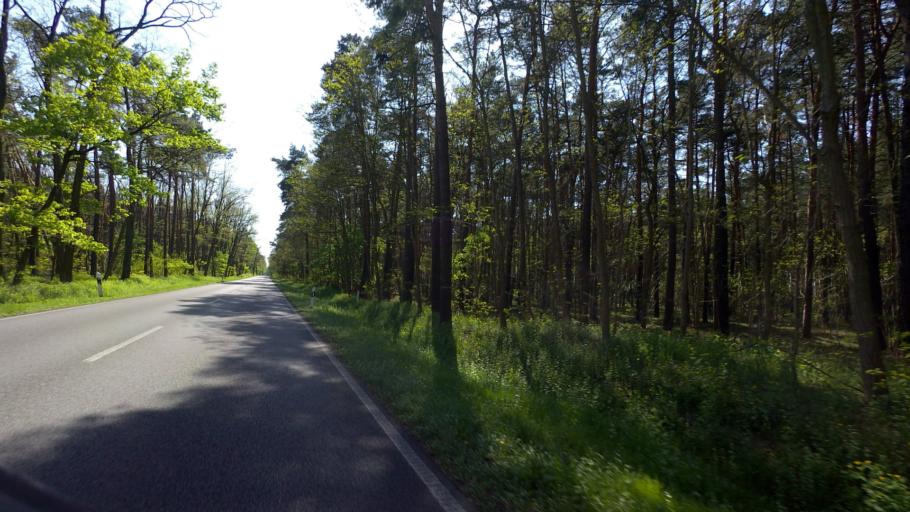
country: DE
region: Brandenburg
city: Tauche
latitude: 52.1288
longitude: 14.1981
